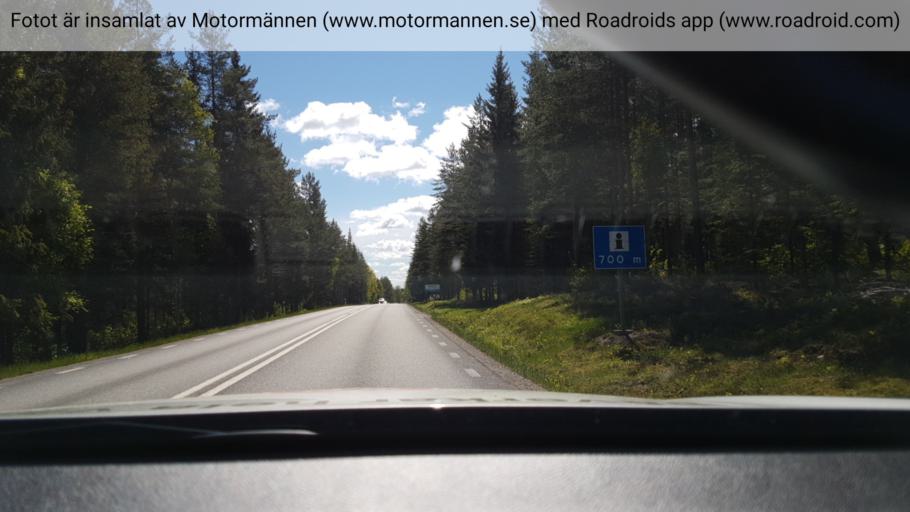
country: SE
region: Dalarna
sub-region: Faluns Kommun
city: Bjursas
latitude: 60.7373
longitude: 15.4326
